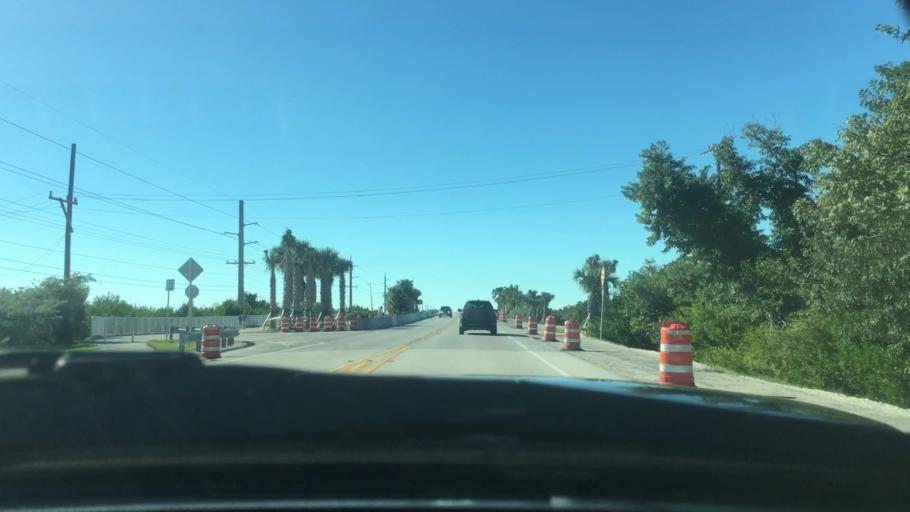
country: US
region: Florida
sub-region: Monroe County
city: Cudjoe Key
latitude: 24.6629
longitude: -81.4641
